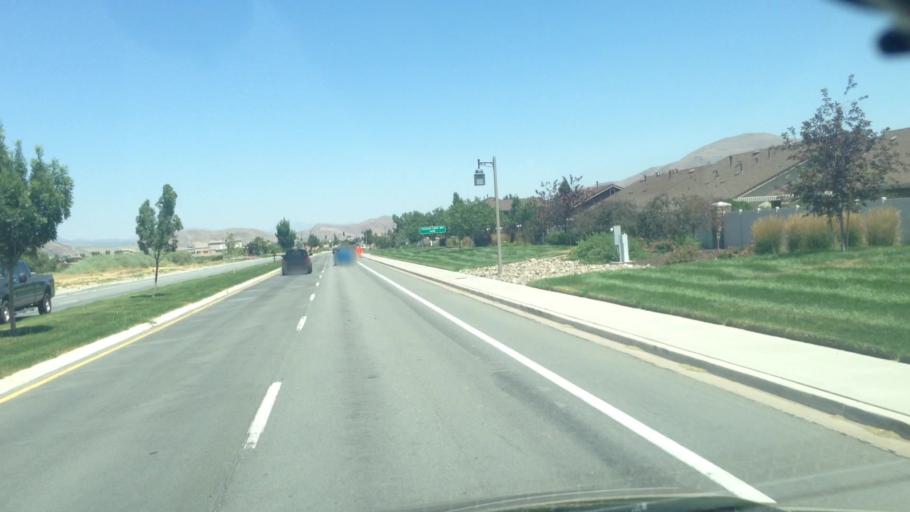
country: US
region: Nevada
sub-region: Washoe County
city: Sparks
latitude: 39.4127
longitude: -119.7333
